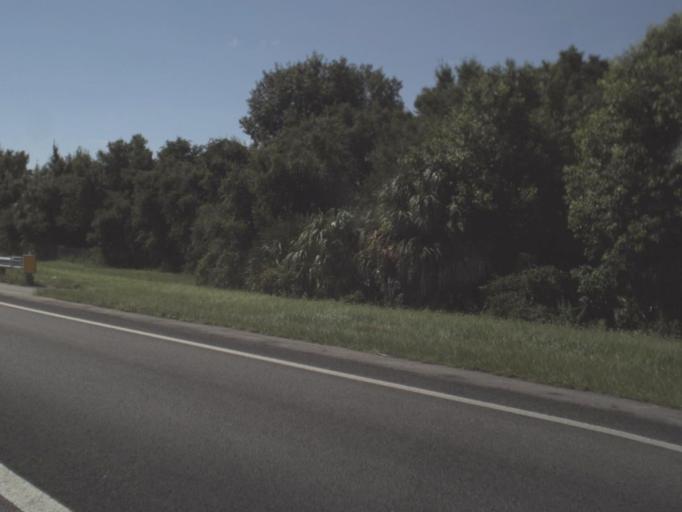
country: US
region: Florida
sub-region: Charlotte County
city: Charlotte Park
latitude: 26.8921
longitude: -81.9994
